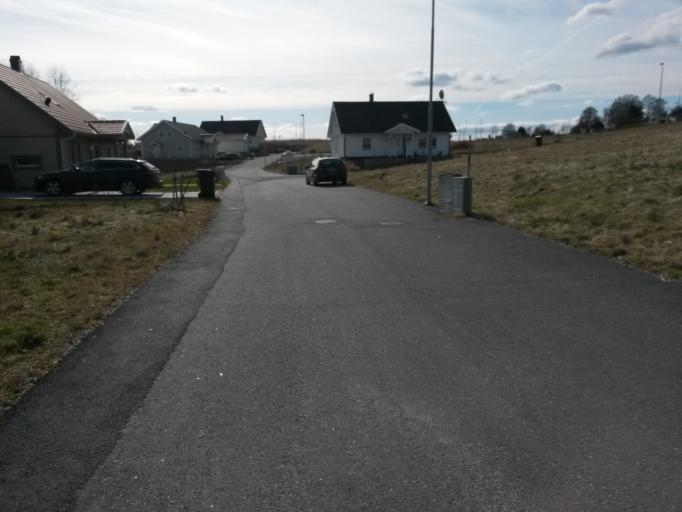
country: SE
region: Vaestra Goetaland
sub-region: Vargarda Kommun
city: Vargarda
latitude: 58.0249
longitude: 12.8062
